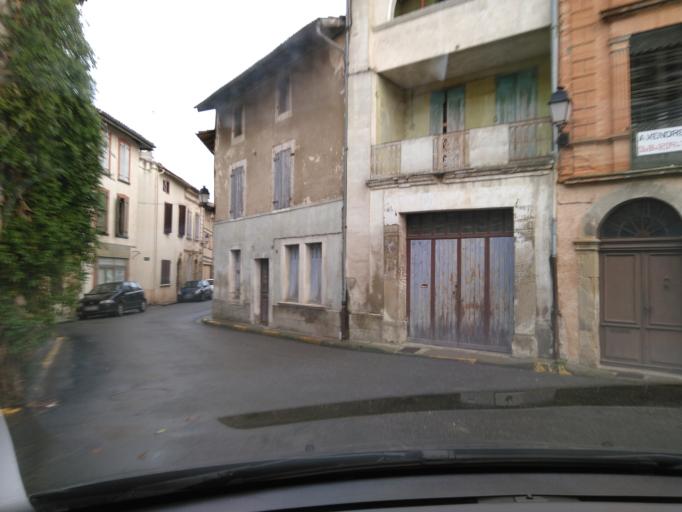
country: FR
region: Midi-Pyrenees
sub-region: Departement de la Haute-Garonne
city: Montesquieu-Volvestre
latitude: 43.1429
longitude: 1.3078
